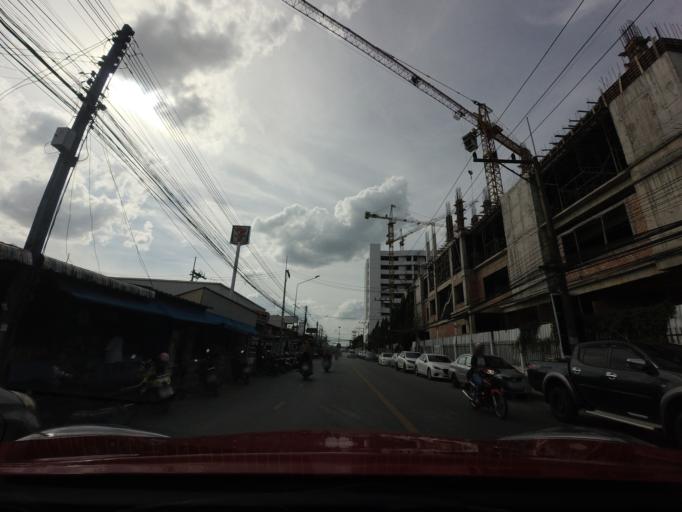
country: TH
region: Yala
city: Yala
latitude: 6.5463
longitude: 101.2767
